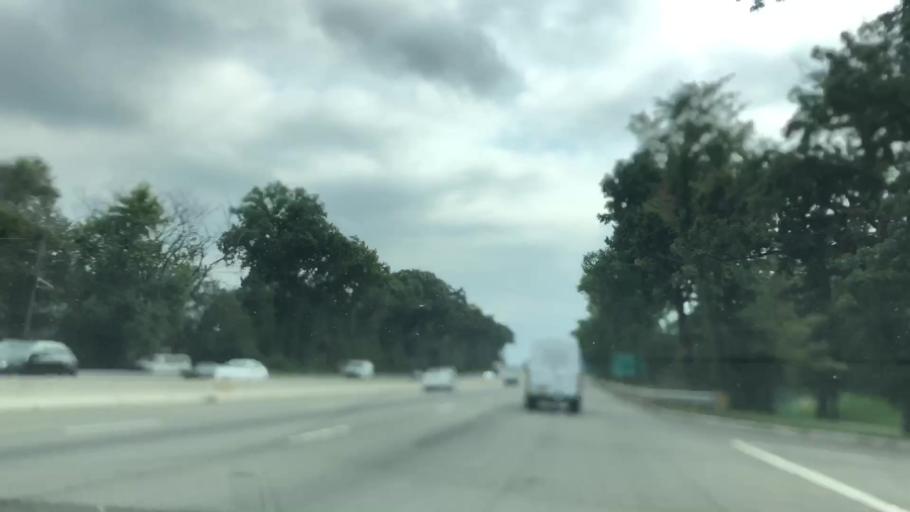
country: US
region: New Jersey
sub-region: Passaic County
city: Clifton
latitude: 40.8483
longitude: -74.1718
